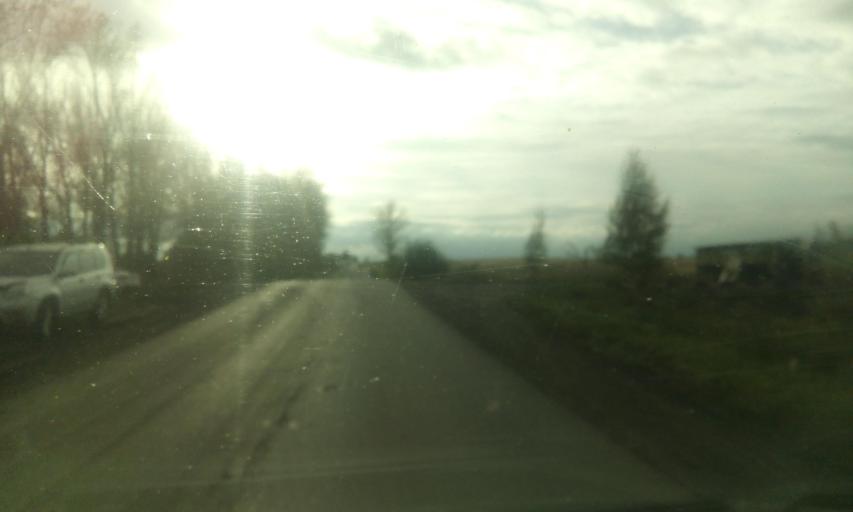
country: RU
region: Tula
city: Partizan
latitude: 53.9713
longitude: 38.1136
